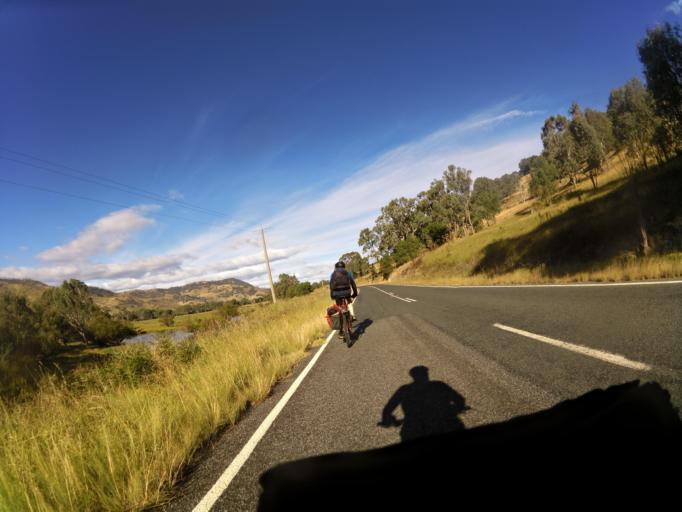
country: AU
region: New South Wales
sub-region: Greater Hume Shire
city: Holbrook
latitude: -35.9695
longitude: 147.7769
